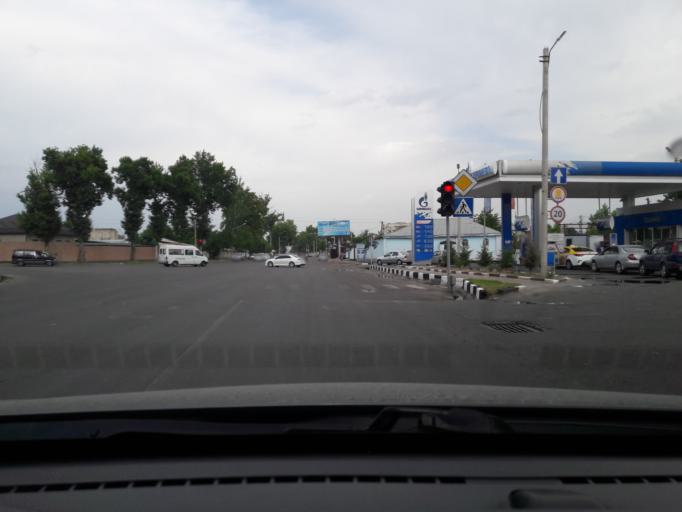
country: TJ
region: Dushanbe
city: Dushanbe
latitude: 38.5462
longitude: 68.7475
